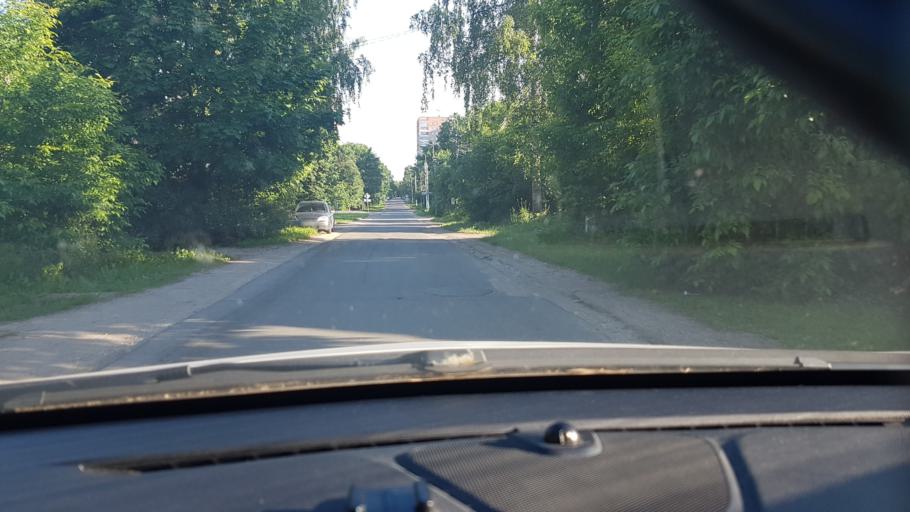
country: RU
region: Moskovskaya
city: Istra
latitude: 55.9181
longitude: 36.8702
